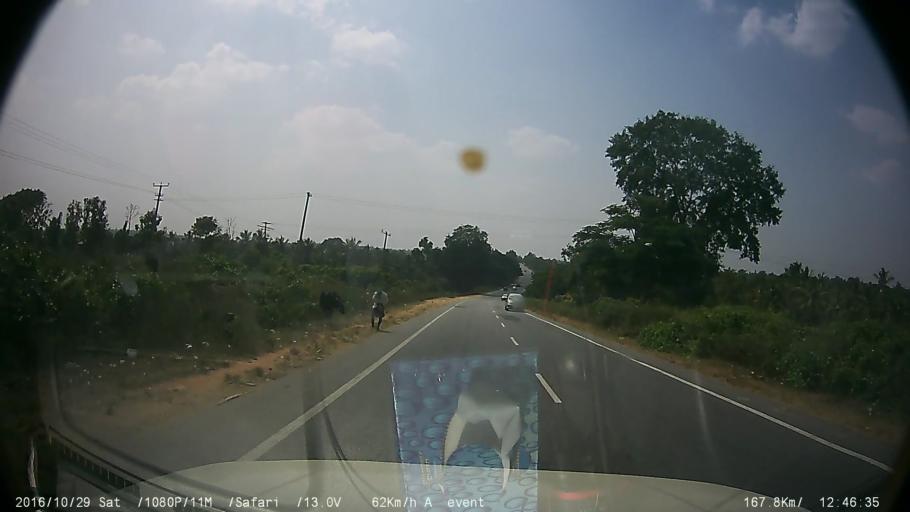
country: IN
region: Karnataka
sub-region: Mysore
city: Hunsur
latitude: 12.3394
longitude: 76.3948
